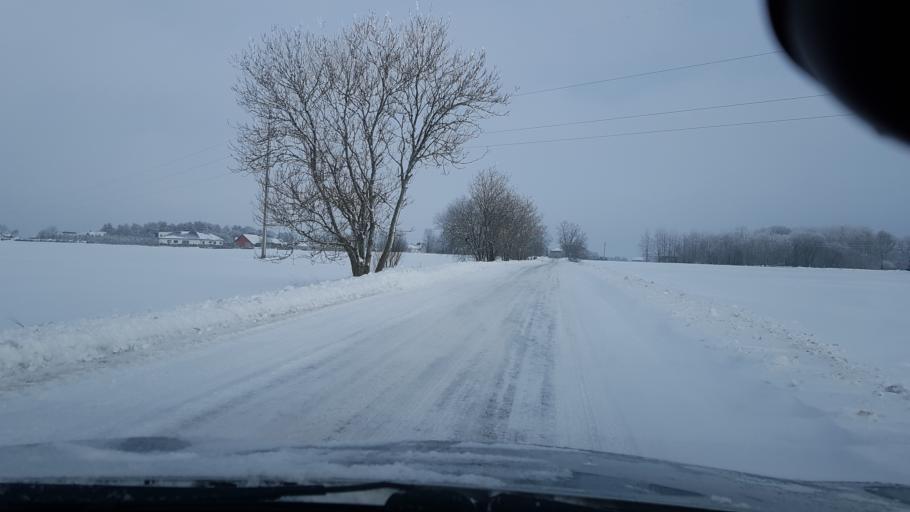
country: EE
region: Harju
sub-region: Keila linn
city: Keila
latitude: 59.3339
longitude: 24.4453
